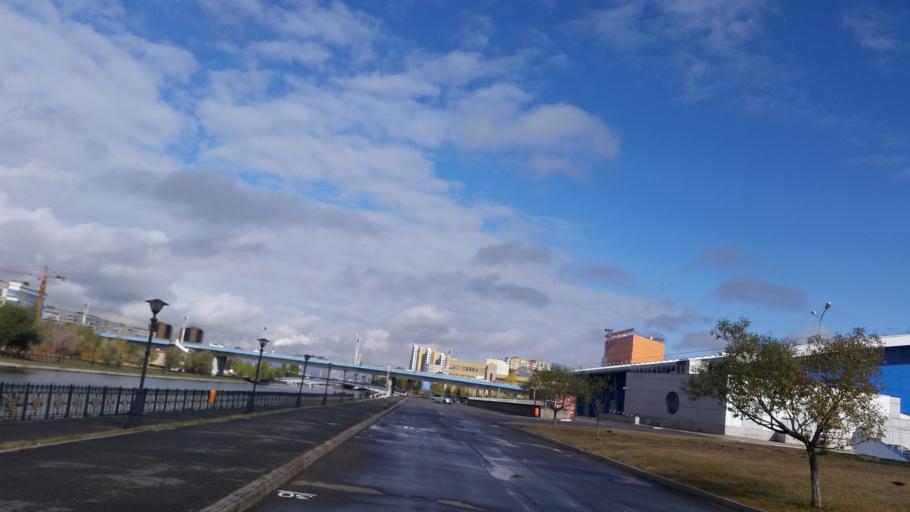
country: KZ
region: Astana Qalasy
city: Astana
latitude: 51.1567
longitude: 71.4628
